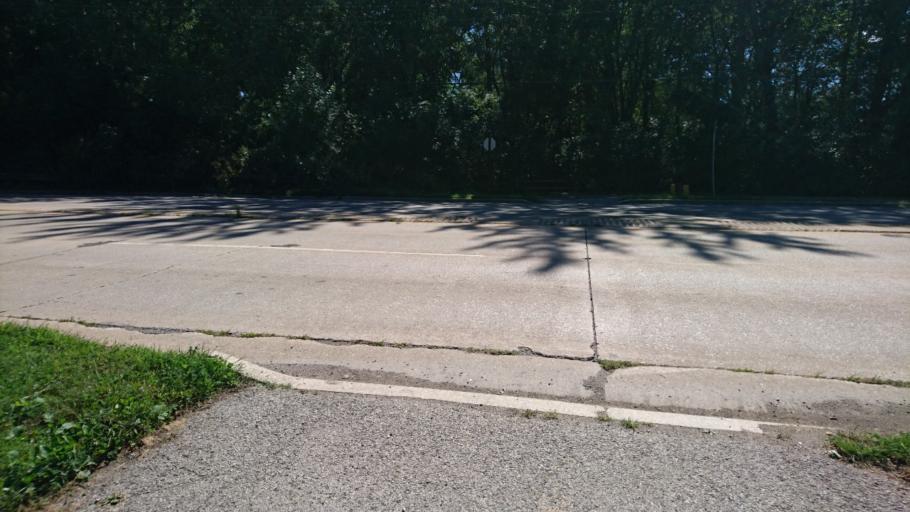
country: US
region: Illinois
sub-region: Cook County
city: Chicago Heights
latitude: 41.5208
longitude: -87.6273
